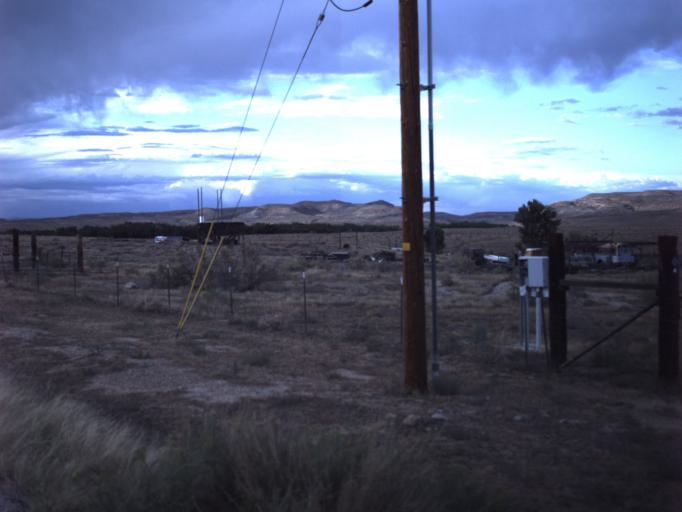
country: US
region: Utah
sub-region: Grand County
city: Moab
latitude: 38.8486
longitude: -109.2831
